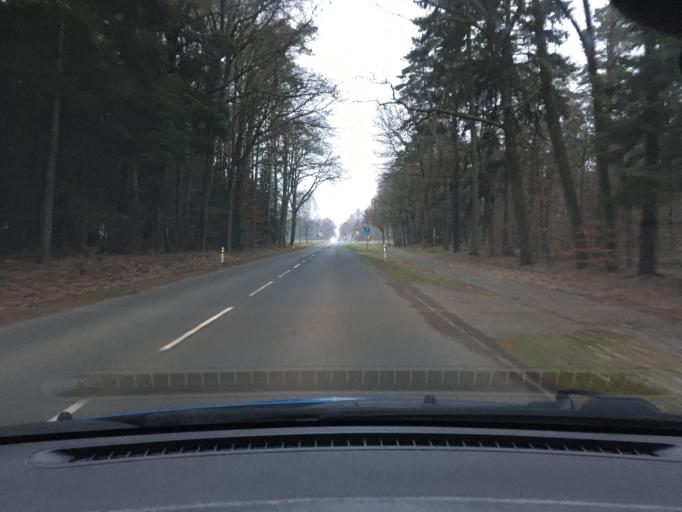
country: DE
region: Lower Saxony
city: Bispingen
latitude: 53.1191
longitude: 9.9522
